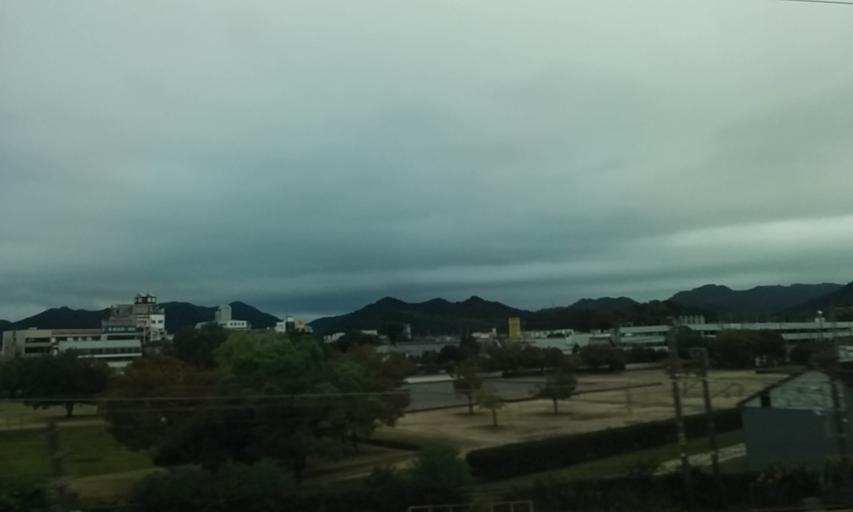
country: JP
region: Hyogo
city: Himeji
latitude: 34.8194
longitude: 134.7305
